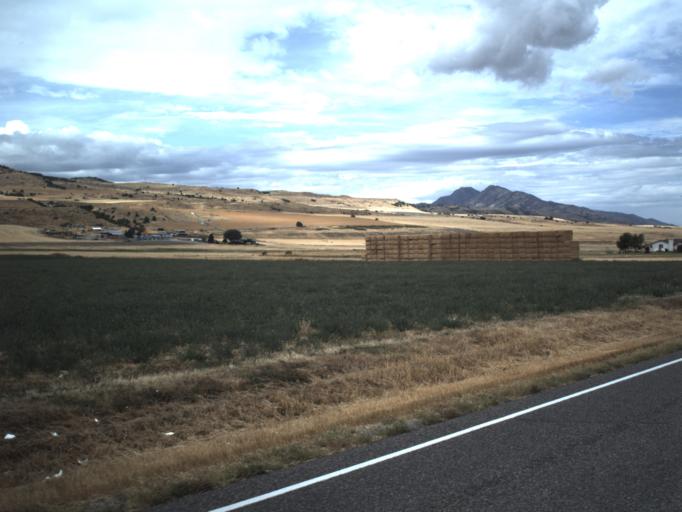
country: US
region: Utah
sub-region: Cache County
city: Benson
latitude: 41.8189
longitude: -111.9977
